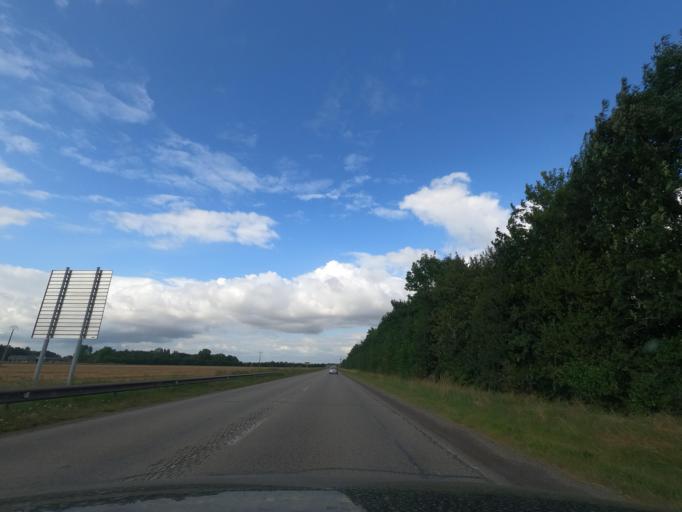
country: FR
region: Haute-Normandie
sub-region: Departement de l'Eure
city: Broglie
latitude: 48.9993
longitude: 0.5104
